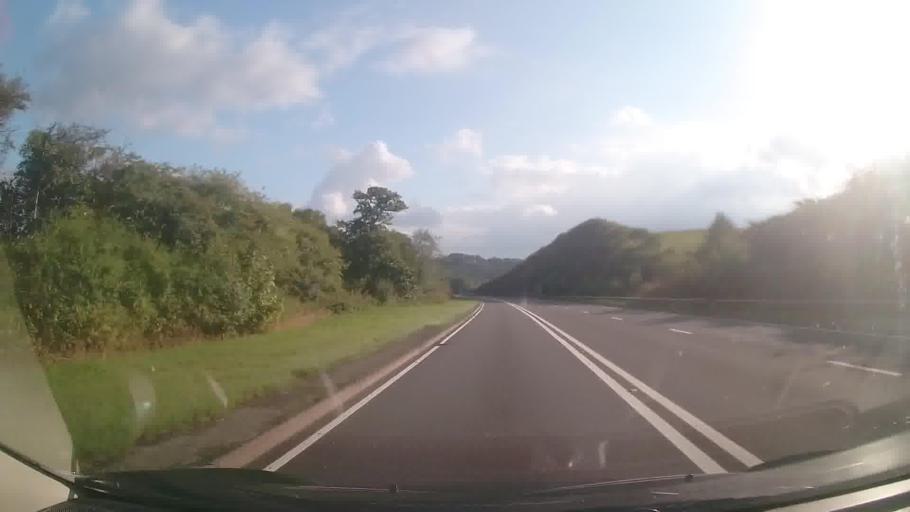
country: GB
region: Wales
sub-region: Pembrokeshire
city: Kilgetty
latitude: 51.7418
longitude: -4.7016
